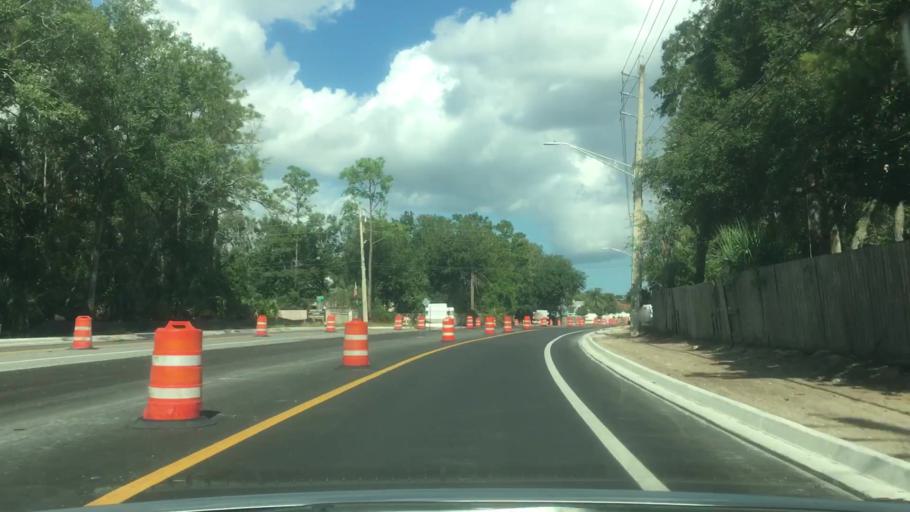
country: US
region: Florida
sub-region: Duval County
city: Atlantic Beach
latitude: 30.3280
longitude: -81.4716
